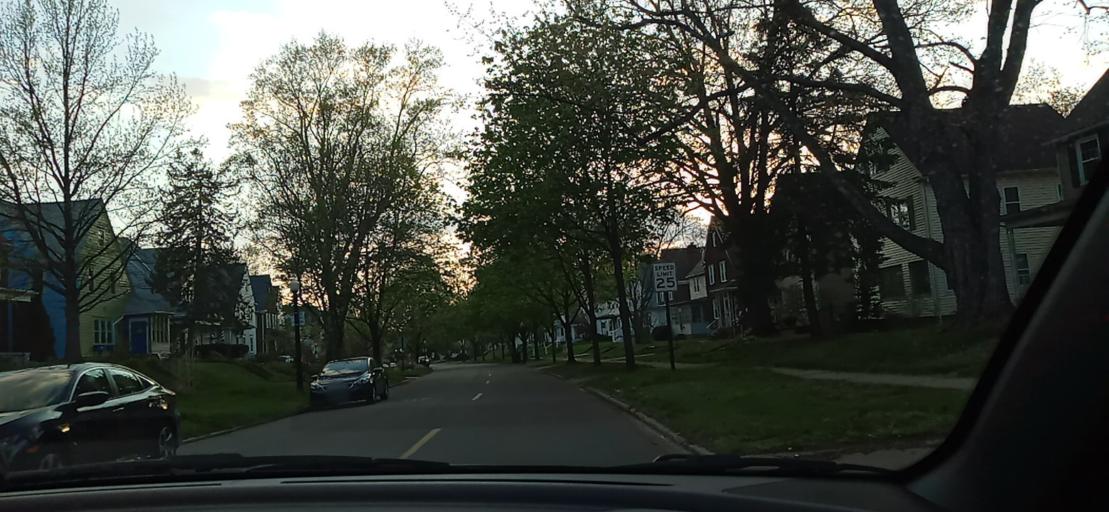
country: US
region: Ohio
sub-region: Summit County
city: Akron
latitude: 41.0447
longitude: -81.5127
